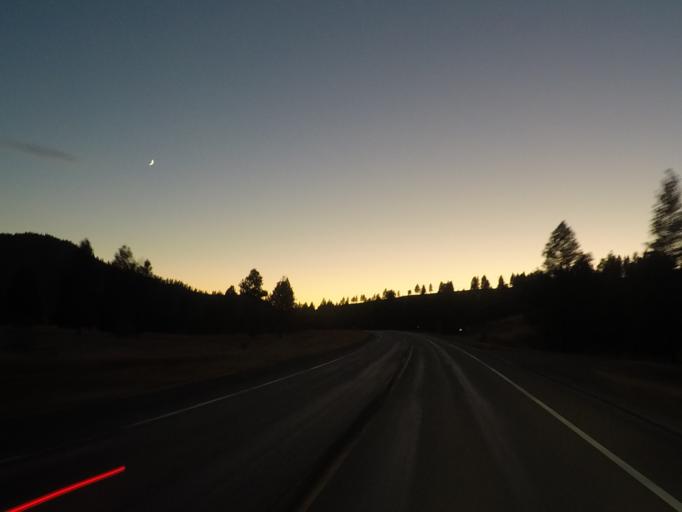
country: US
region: Montana
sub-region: Missoula County
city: Seeley Lake
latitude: 47.0295
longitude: -113.2813
